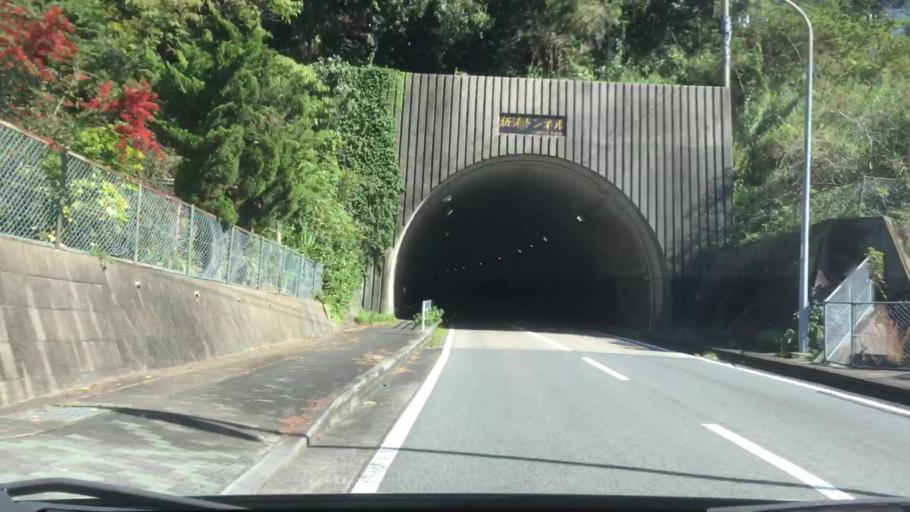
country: JP
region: Nagasaki
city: Sasebo
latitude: 32.9496
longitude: 129.6408
